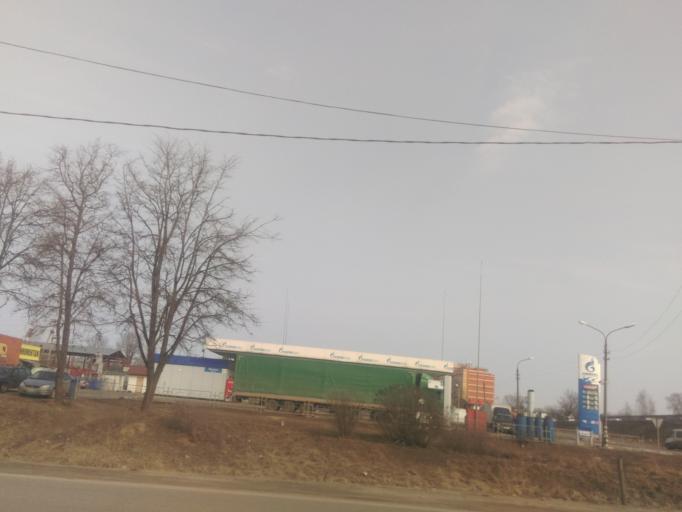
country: RU
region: Moskovskaya
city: Kubinka
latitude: 55.5710
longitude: 36.6954
